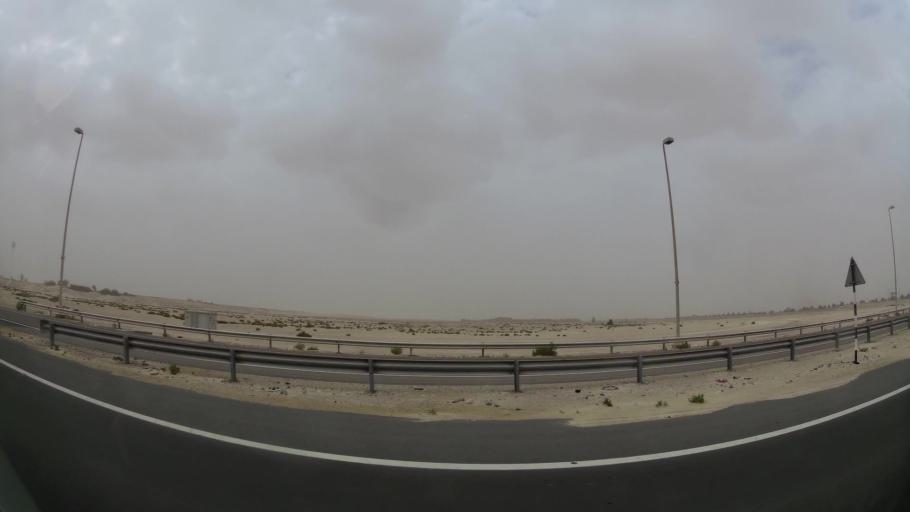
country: AE
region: Abu Dhabi
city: Abu Dhabi
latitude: 24.4087
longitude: 54.7156
